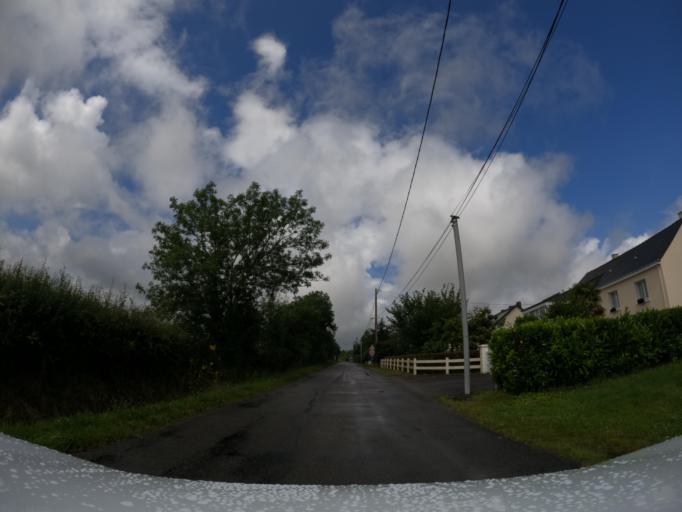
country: FR
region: Pays de la Loire
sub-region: Departement de la Loire-Atlantique
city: Ligne
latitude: 47.3975
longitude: -1.3810
